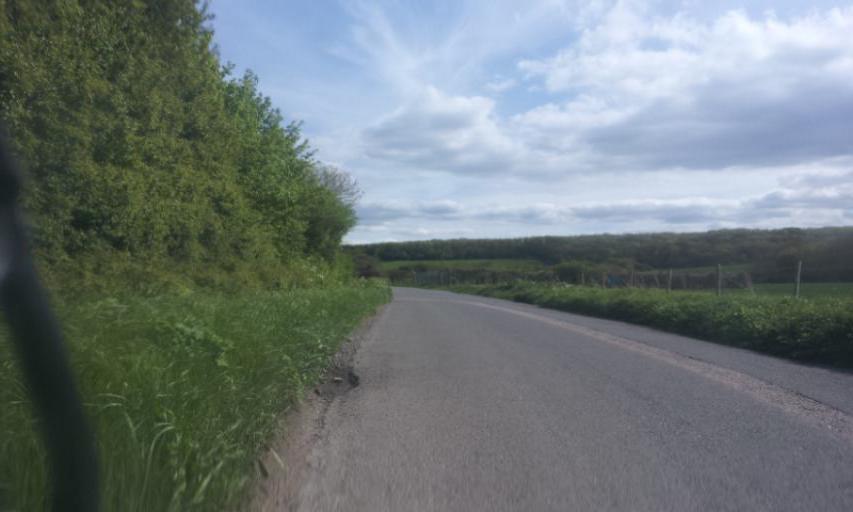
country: GB
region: England
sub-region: Medway
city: Cuxton
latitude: 51.3790
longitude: 0.4245
